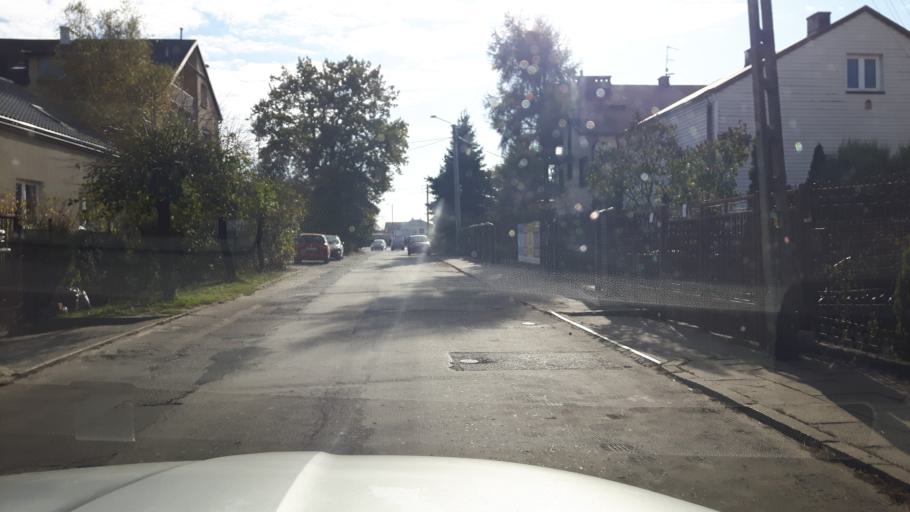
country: PL
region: Masovian Voivodeship
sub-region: Powiat wolominski
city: Zabki
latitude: 52.2956
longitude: 21.1000
